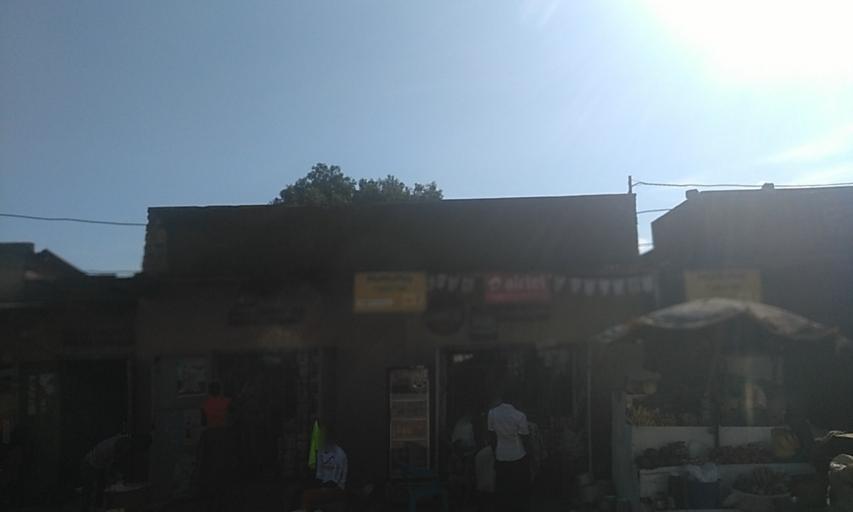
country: UG
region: Central Region
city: Kampala Central Division
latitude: 0.3295
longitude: 32.5323
